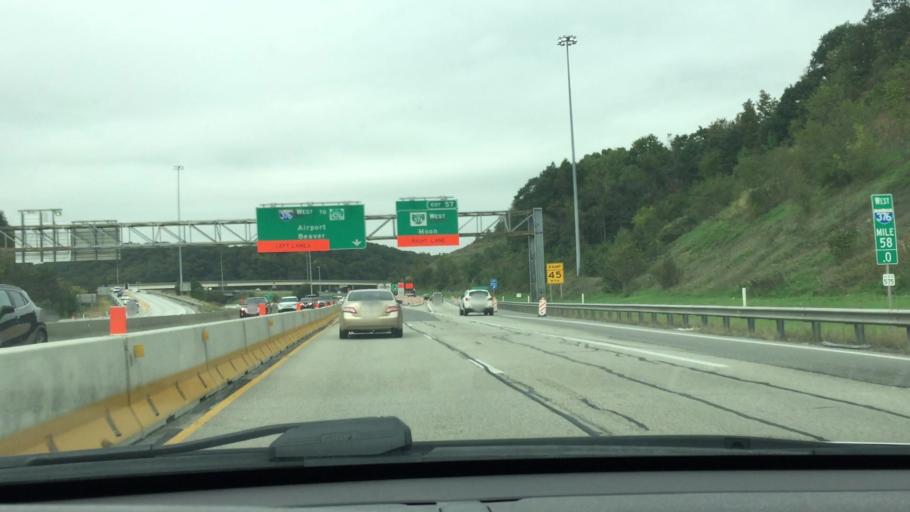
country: US
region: Pennsylvania
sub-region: Allegheny County
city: Enlow
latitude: 40.4643
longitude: -80.1946
